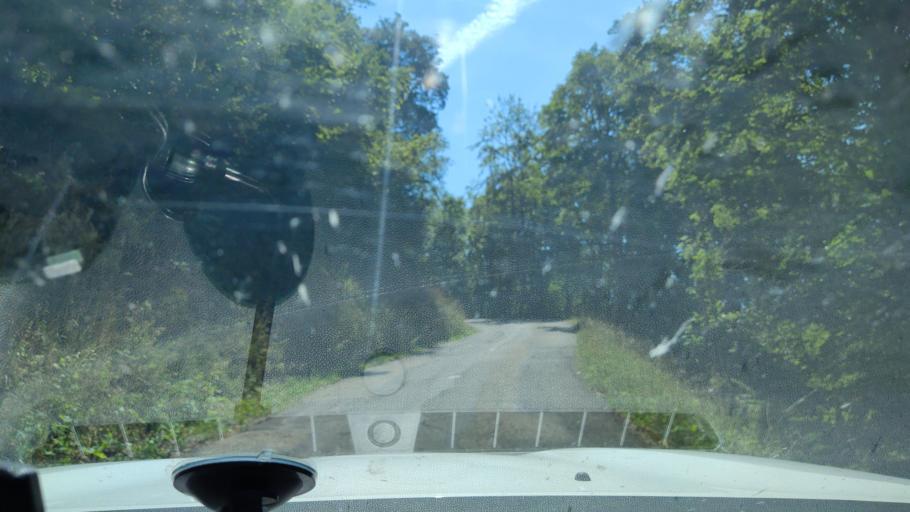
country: FR
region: Rhone-Alpes
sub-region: Departement de la Savoie
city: Le Bourget-du-Lac
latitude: 45.6455
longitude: 5.8097
